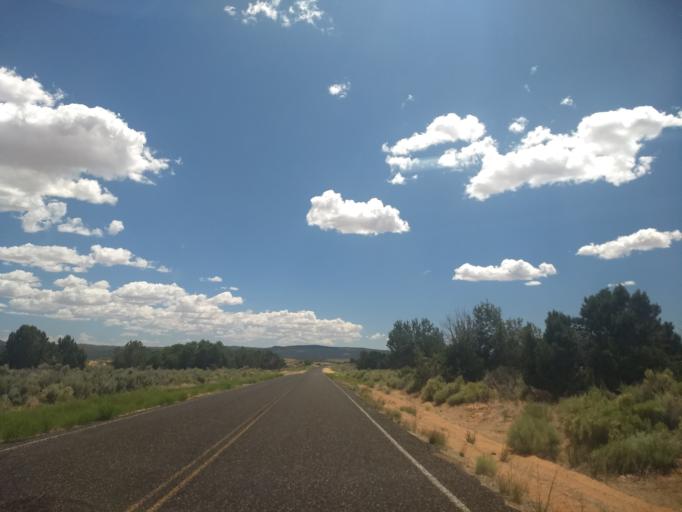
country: US
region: Utah
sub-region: Kane County
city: Kanab
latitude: 37.0460
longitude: -112.7218
